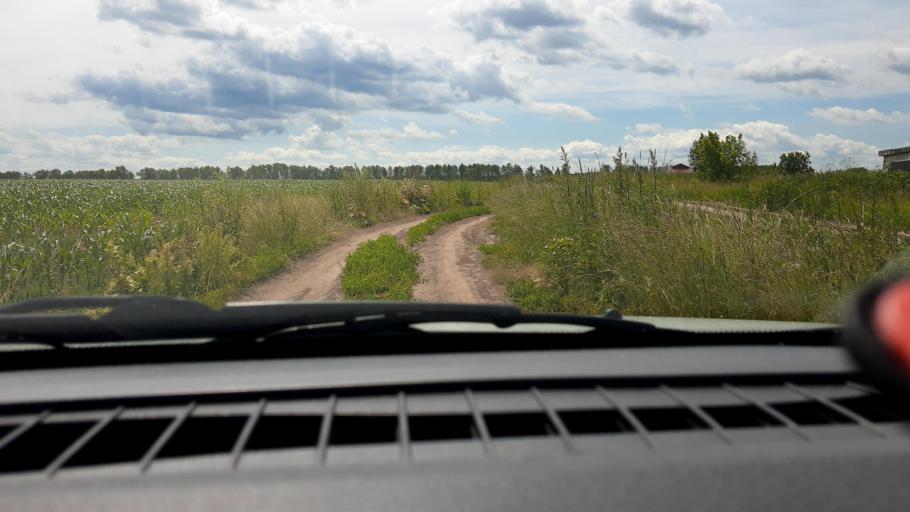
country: RU
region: Nizjnij Novgorod
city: Afonino
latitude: 56.1252
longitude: 44.0315
